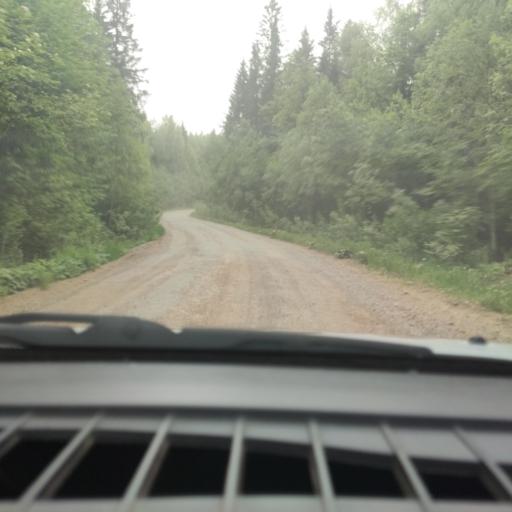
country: RU
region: Perm
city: Novyye Lyady
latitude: 57.9017
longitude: 56.6524
